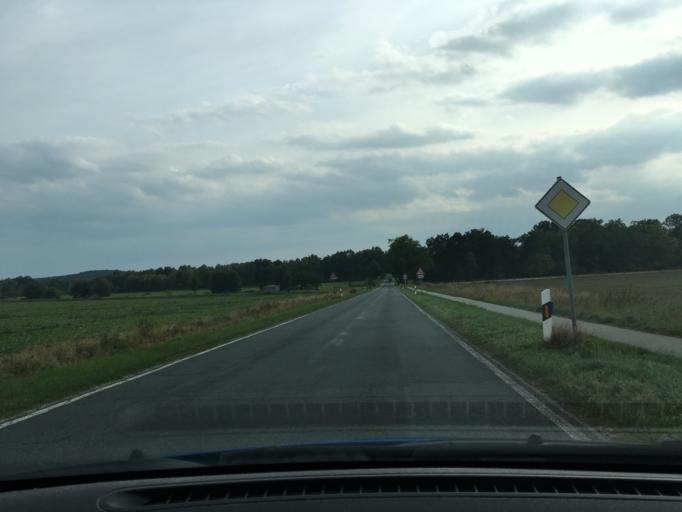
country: DE
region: Lower Saxony
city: Asendorf
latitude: 53.2863
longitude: 9.9776
